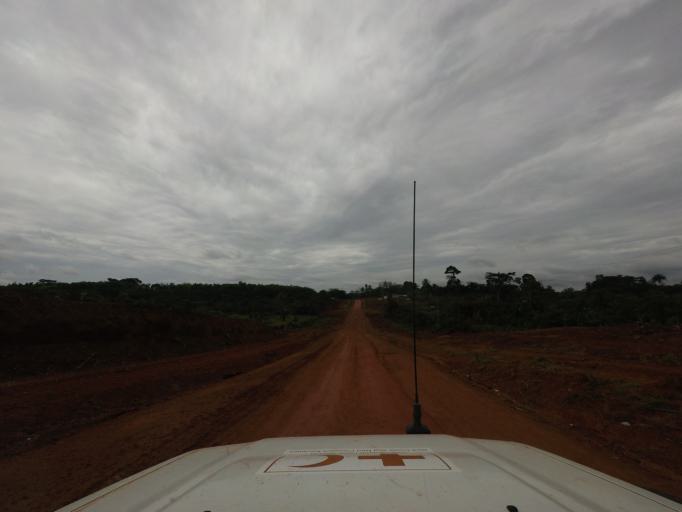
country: LR
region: Nimba
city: Sanniquellie
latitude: 7.2294
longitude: -8.9160
